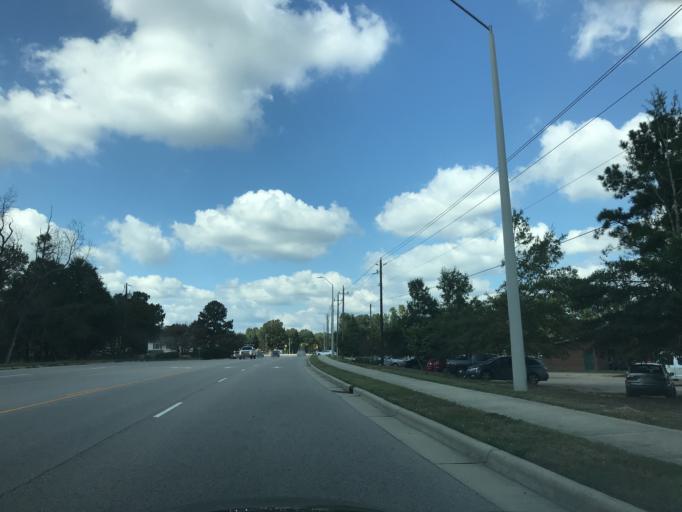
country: US
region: North Carolina
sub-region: Wake County
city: Rolesville
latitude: 35.8836
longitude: -78.5515
